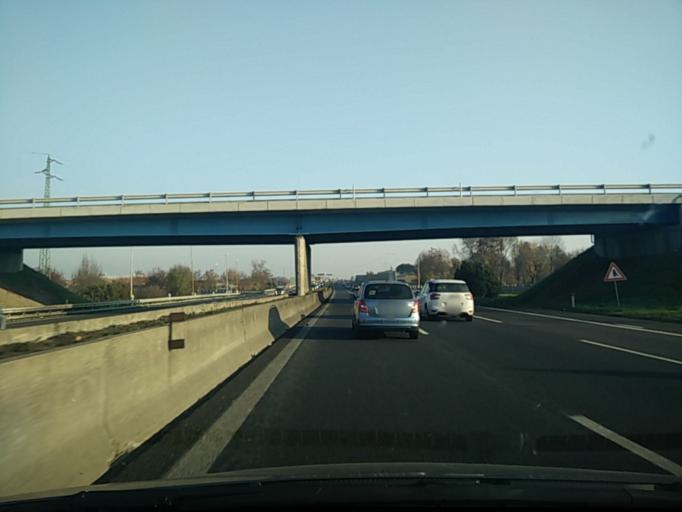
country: IT
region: Lombardy
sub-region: Provincia di Bergamo
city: Telgate
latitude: 45.6332
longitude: 9.8545
